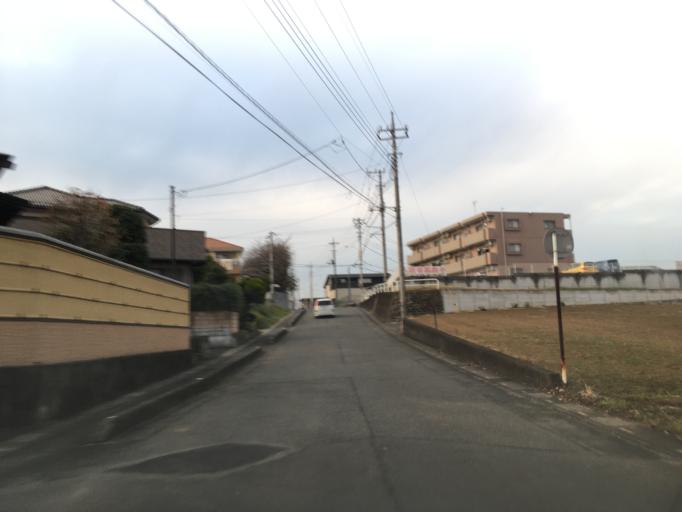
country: JP
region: Saitama
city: Sayama
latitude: 35.8970
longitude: 139.3757
